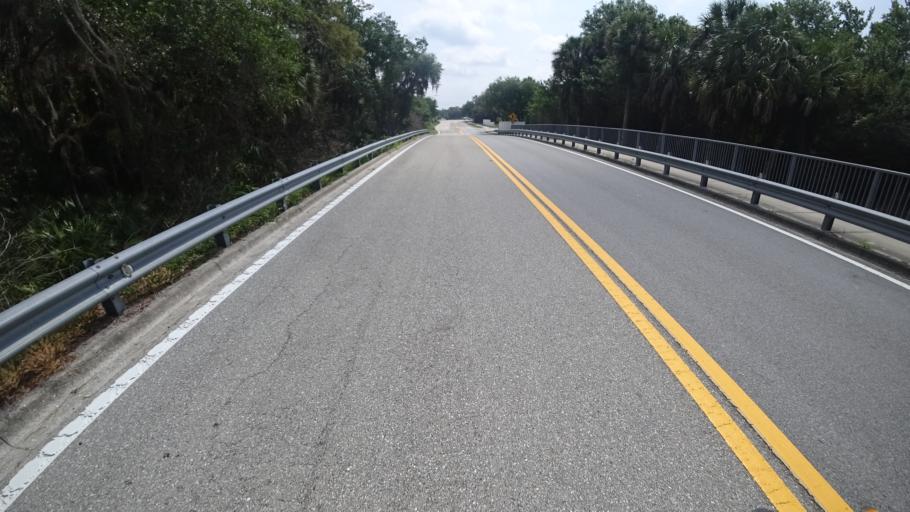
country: US
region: Florida
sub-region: Sarasota County
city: North Sarasota
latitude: 27.4180
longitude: -82.5077
